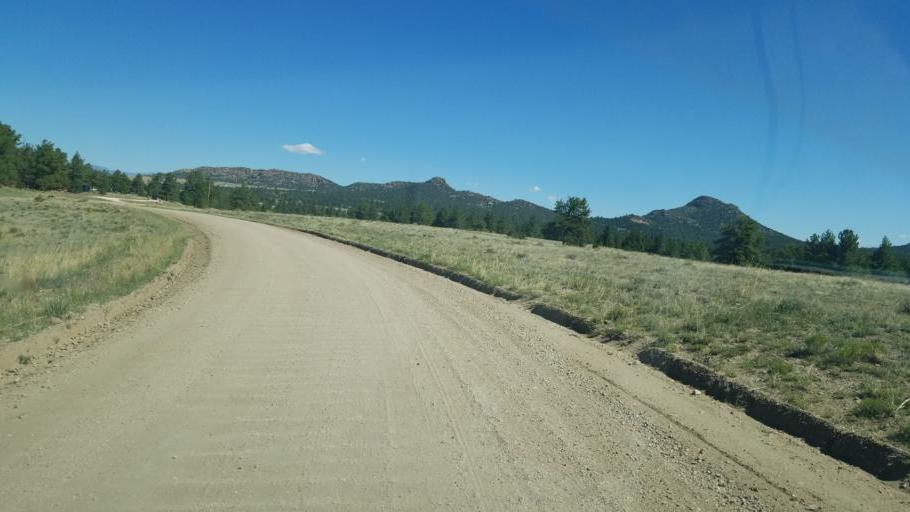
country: US
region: Colorado
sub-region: Custer County
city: Westcliffe
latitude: 38.2034
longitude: -105.4431
